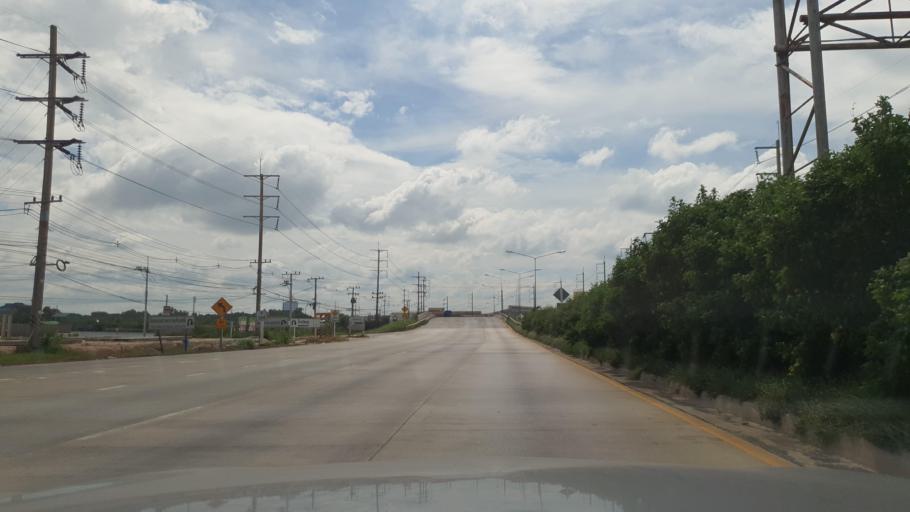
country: TH
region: Chachoengsao
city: Bang Pakong
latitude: 13.5549
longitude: 100.9920
